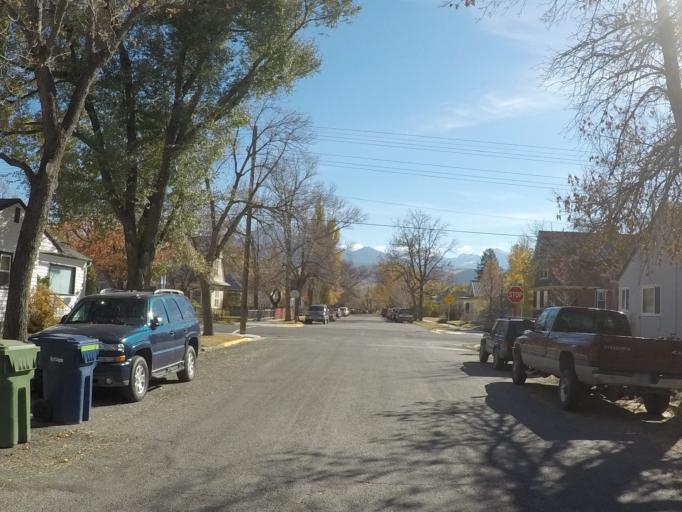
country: US
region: Montana
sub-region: Park County
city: Livingston
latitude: 45.6562
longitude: -110.5616
